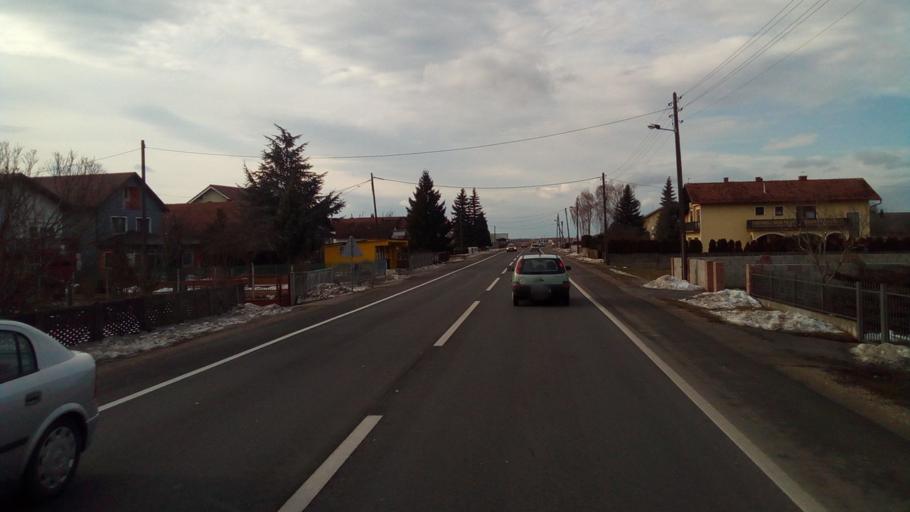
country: HR
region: Medimurska
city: Kursanec
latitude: 46.2993
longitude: 16.3939
